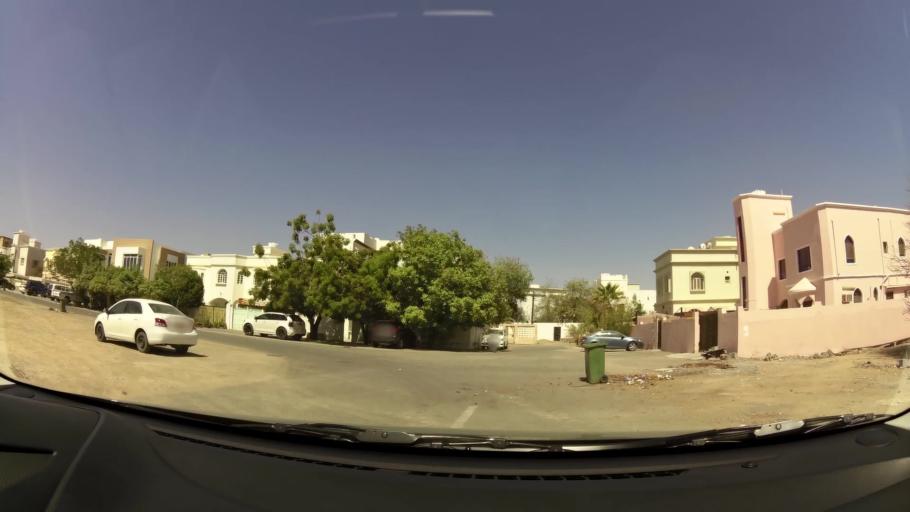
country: OM
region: Muhafazat Masqat
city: As Sib al Jadidah
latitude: 23.5937
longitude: 58.2447
